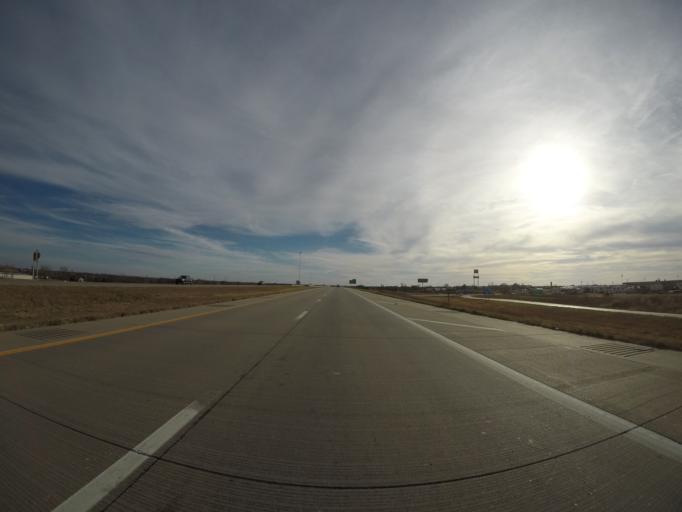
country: US
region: Kansas
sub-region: Franklin County
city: Ottawa
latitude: 38.6253
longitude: -95.2323
